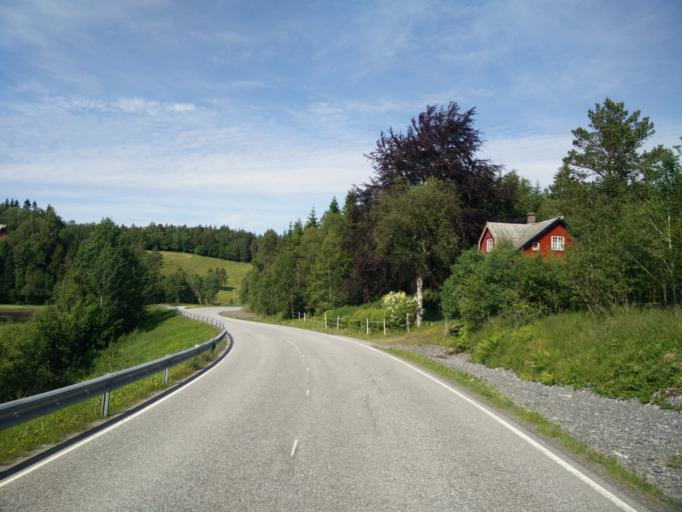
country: NO
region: More og Romsdal
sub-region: Tingvoll
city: Tingvoll
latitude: 63.0278
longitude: 8.0238
